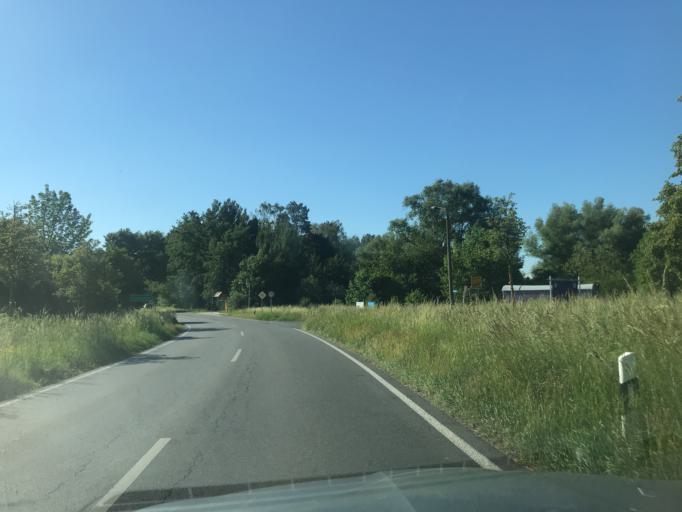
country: DE
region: Brandenburg
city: Bernau bei Berlin
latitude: 52.6463
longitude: 13.6076
